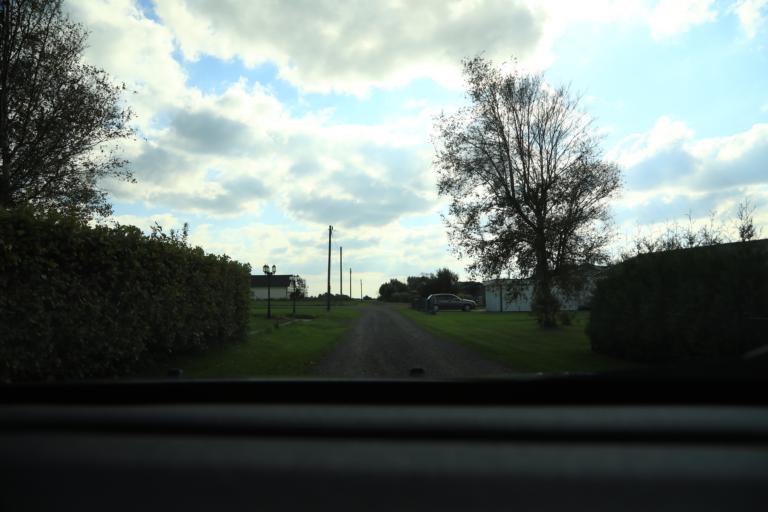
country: SE
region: Halland
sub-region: Varbergs Kommun
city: Tvaaker
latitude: 57.0077
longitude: 12.3584
